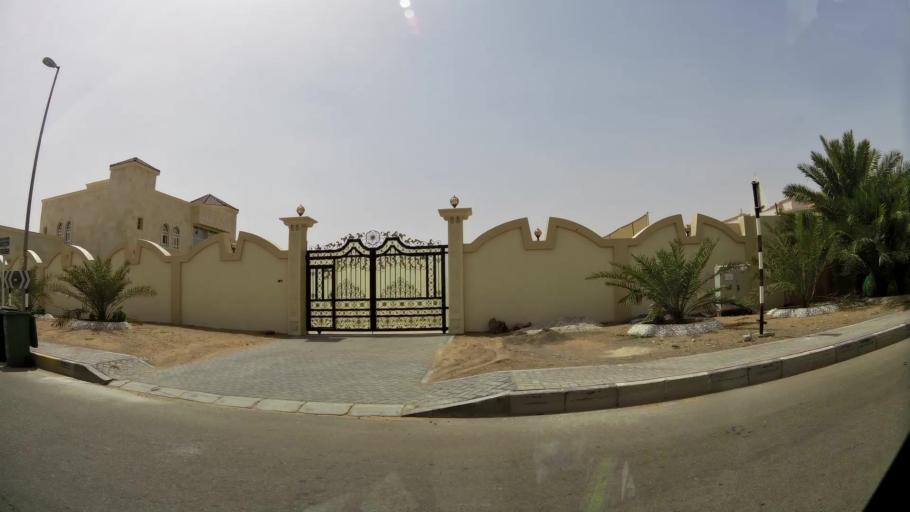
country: AE
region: Abu Dhabi
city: Al Ain
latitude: 24.1558
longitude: 55.6523
